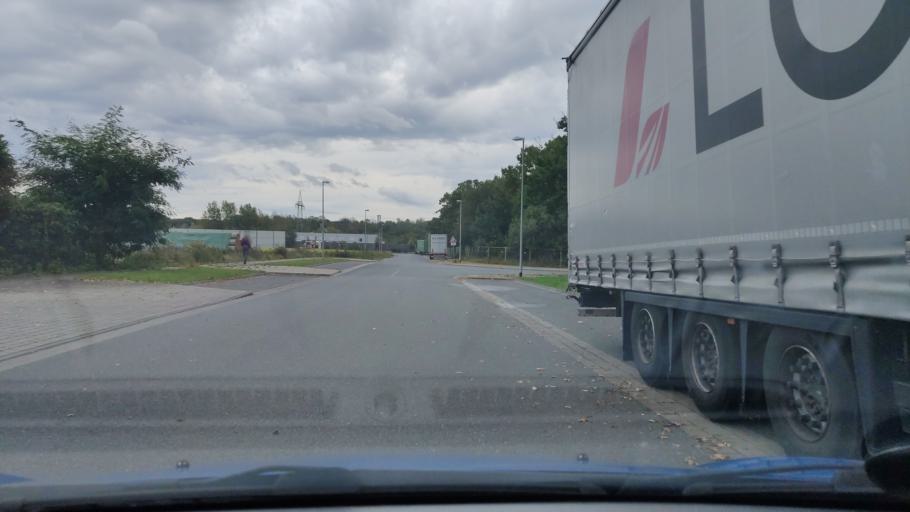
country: DE
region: Lower Saxony
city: Garbsen-Mitte
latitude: 52.4301
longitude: 9.6585
